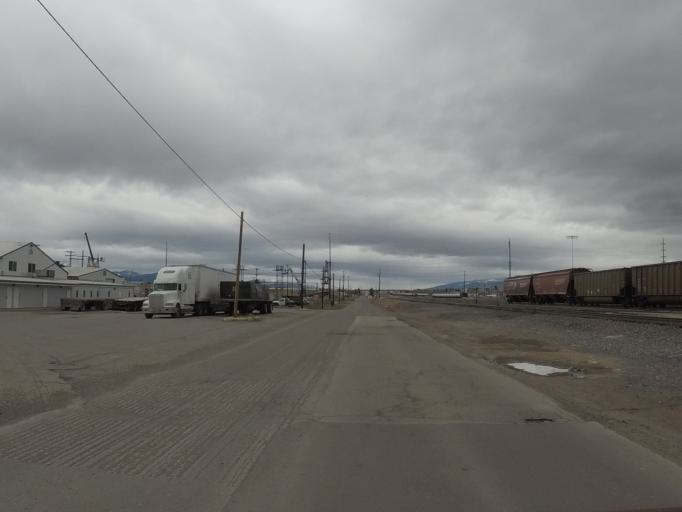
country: US
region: Montana
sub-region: Missoula County
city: Orchard Homes
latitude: 46.8920
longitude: -114.0256
